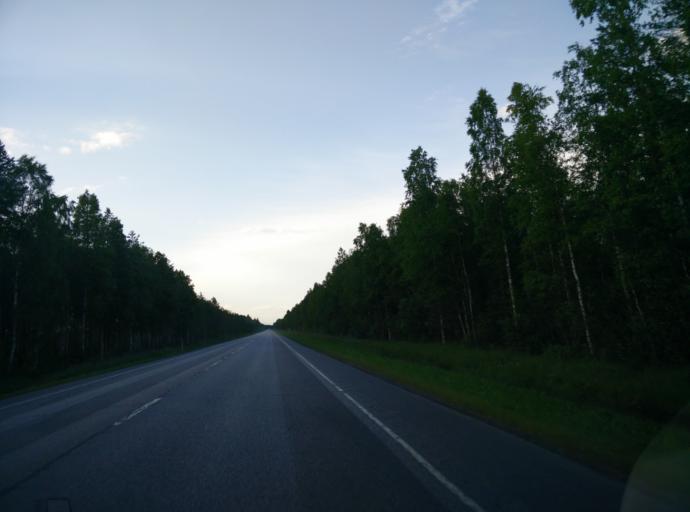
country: FI
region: Northern Ostrobothnia
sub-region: Haapavesi-Siikalatva
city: Pulkkila
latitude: 64.1299
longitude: 25.8001
